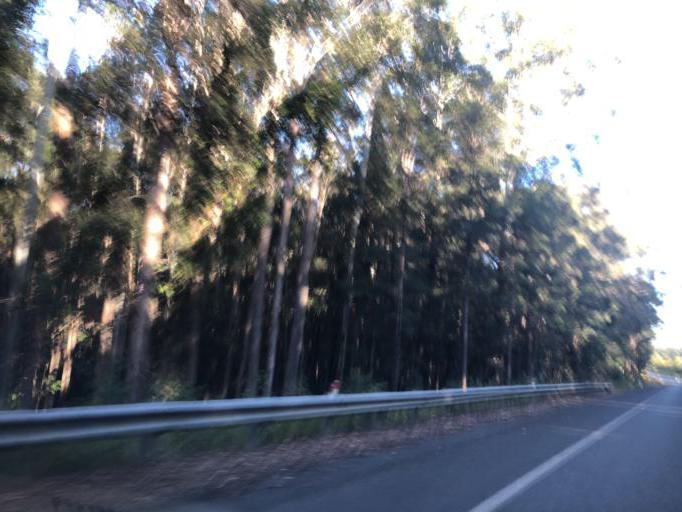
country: AU
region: New South Wales
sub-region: Nambucca Shire
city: Nambucca
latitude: -30.5552
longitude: 153.0063
